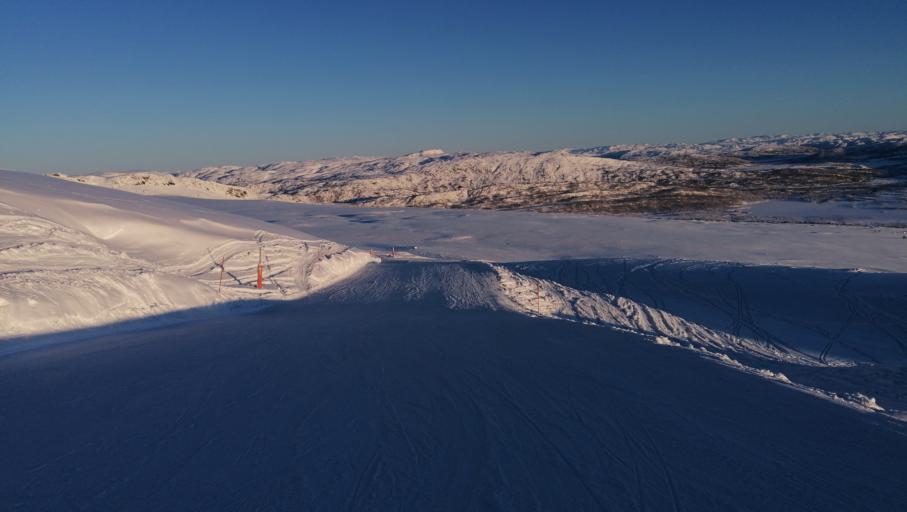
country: NO
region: Aust-Agder
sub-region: Bykle
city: Hovden
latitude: 59.5805
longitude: 7.3314
